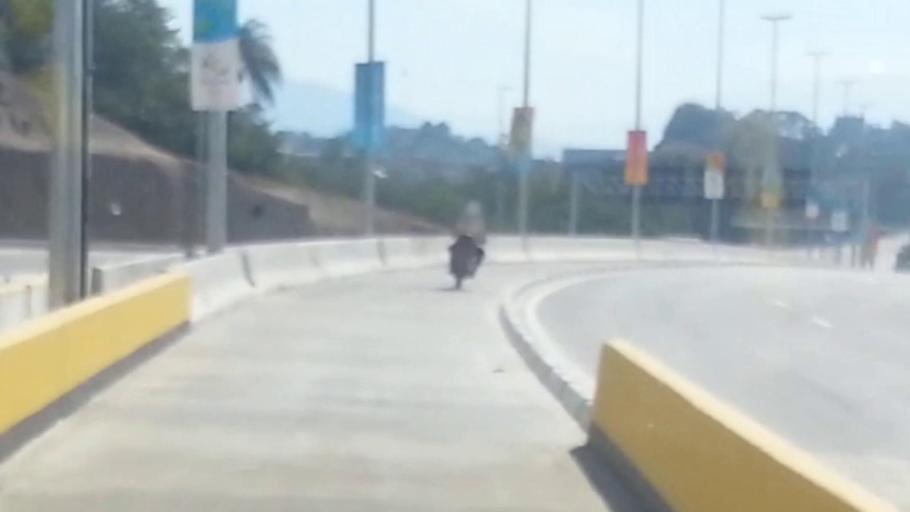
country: BR
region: Rio de Janeiro
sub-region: Nilopolis
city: Nilopolis
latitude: -22.8969
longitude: -43.3987
